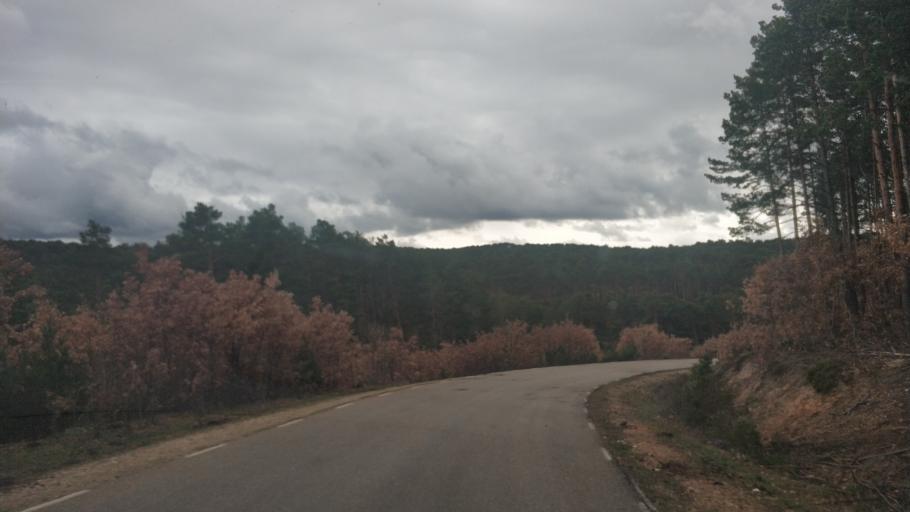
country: ES
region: Castille and Leon
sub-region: Provincia de Burgos
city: Canicosa de la Sierra
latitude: 41.9205
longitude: -3.0378
